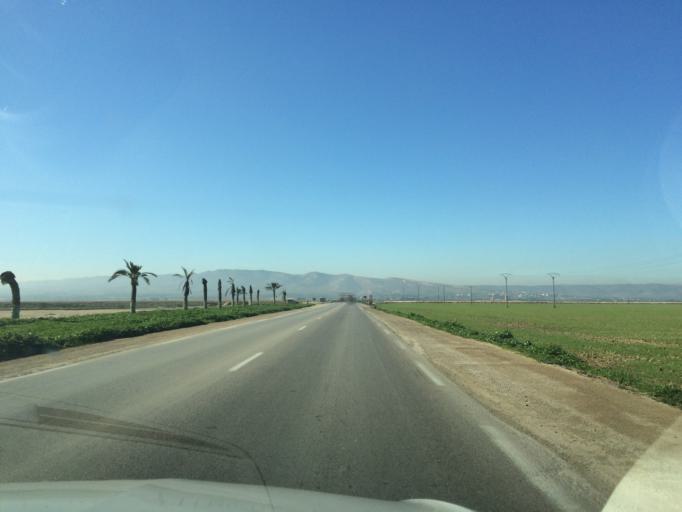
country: DZ
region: Relizane
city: Relizane
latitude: 35.8979
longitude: 0.5677
